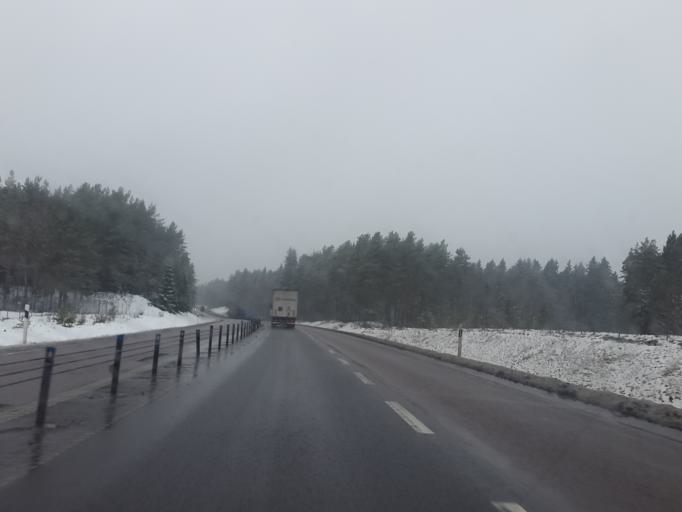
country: SE
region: Joenkoeping
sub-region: Jonkopings Kommun
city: Jonkoping
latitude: 57.7735
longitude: 14.0759
